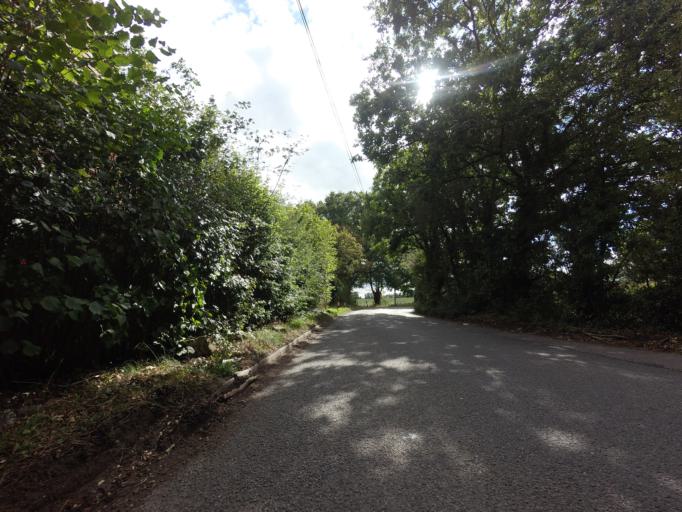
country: GB
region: England
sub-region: Kent
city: Marden
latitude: 51.1597
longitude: 0.4371
